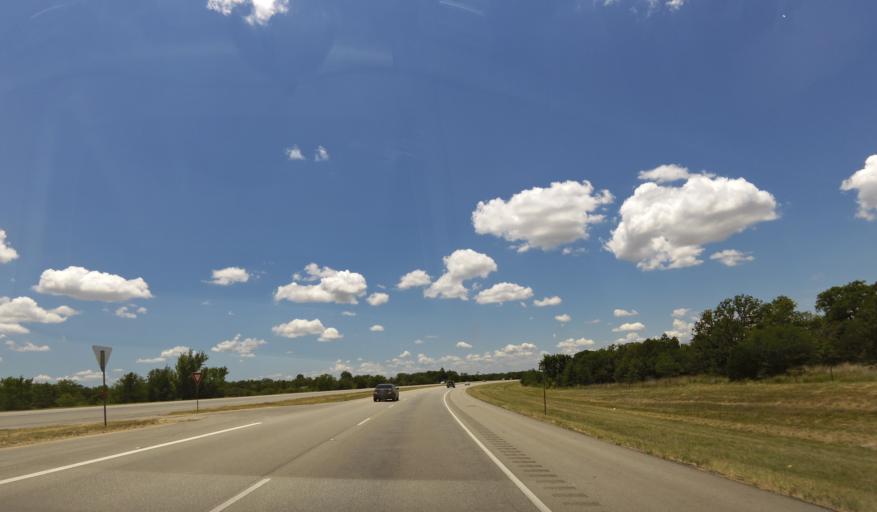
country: US
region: Texas
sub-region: Lee County
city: Giddings
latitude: 30.1408
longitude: -96.7630
